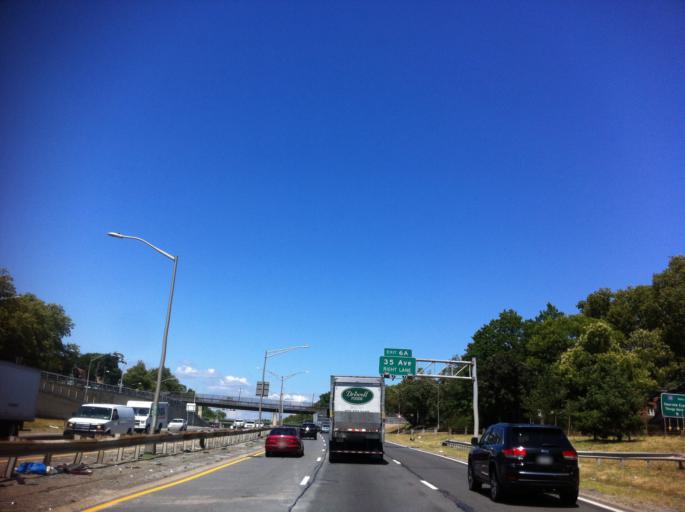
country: US
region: New York
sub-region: Nassau County
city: Bellerose Terrace
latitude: 40.7339
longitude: -73.7665
